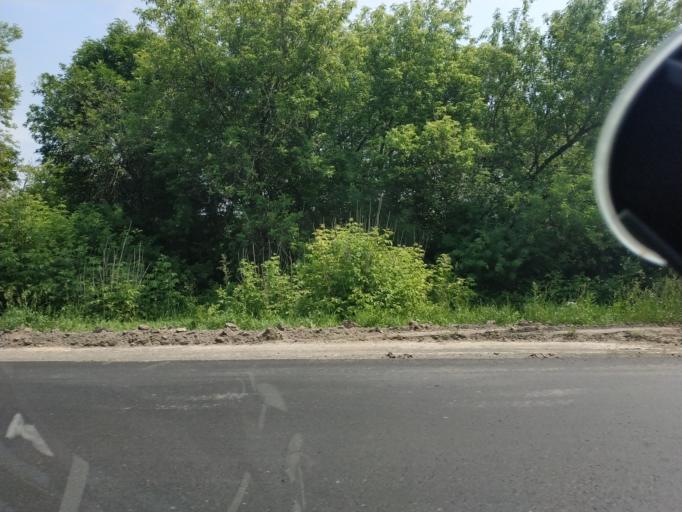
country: RU
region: Moskovskaya
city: Bronnitsy
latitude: 55.3163
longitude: 38.2163
